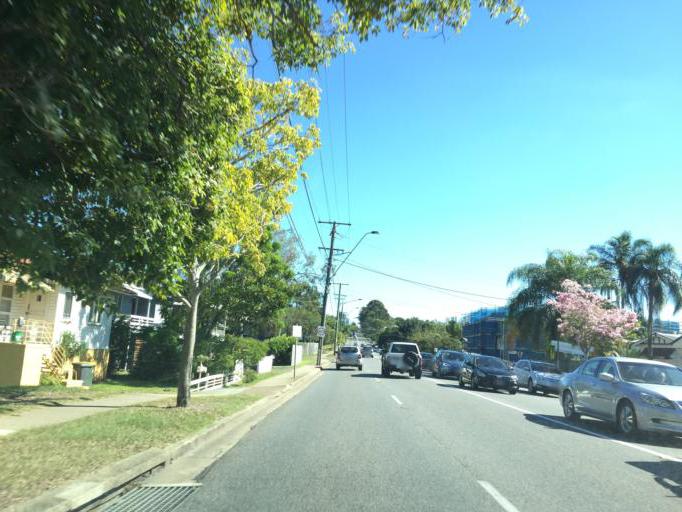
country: AU
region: Queensland
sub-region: Brisbane
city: Everton Park
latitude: -27.4130
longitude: 152.9733
